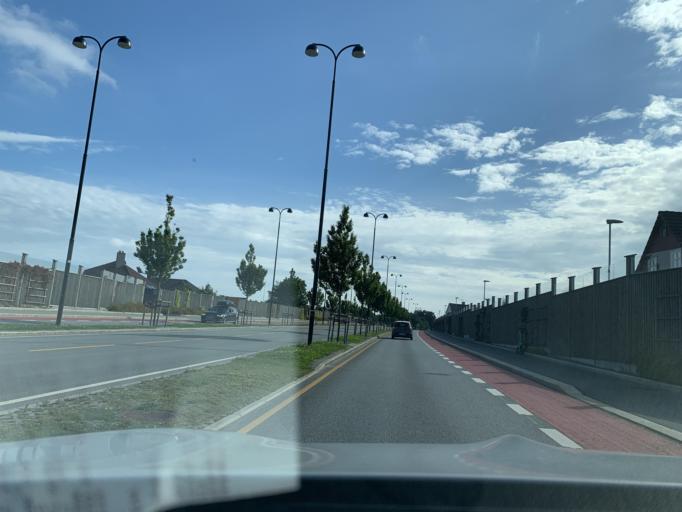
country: NO
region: Rogaland
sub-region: Stavanger
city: Stavanger
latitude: 58.9307
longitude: 5.7375
